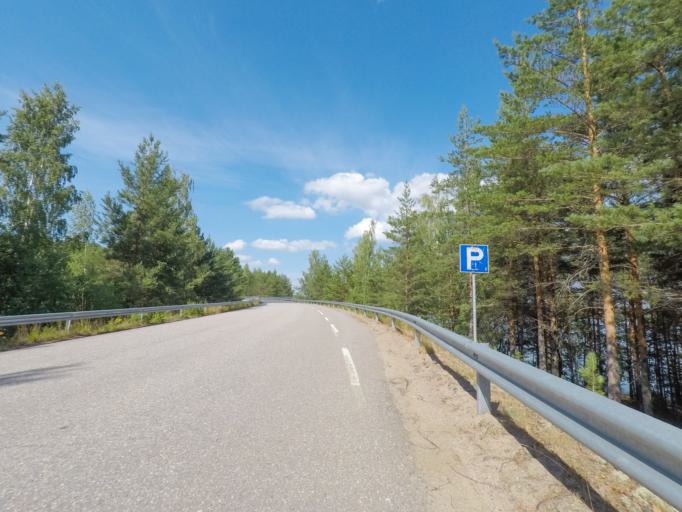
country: FI
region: Southern Savonia
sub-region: Mikkeli
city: Puumala
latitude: 61.4678
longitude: 28.1692
